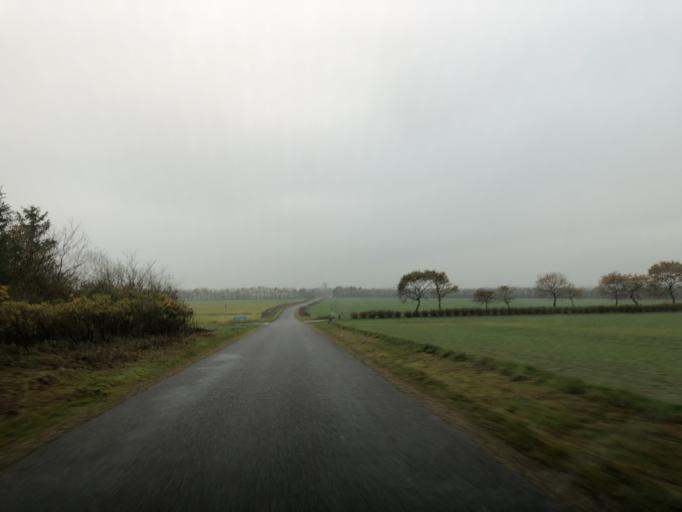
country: DK
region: Central Jutland
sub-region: Herning Kommune
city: Avlum
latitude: 56.2375
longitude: 8.7871
